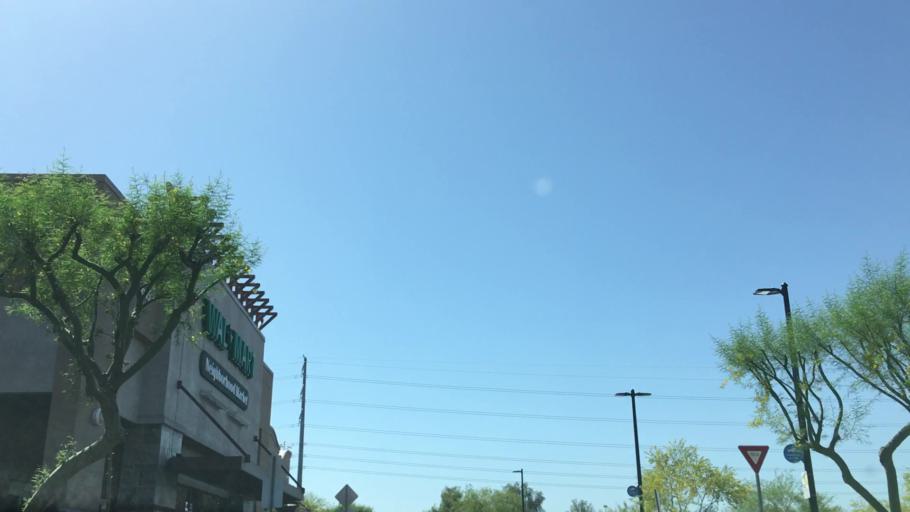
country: US
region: Arizona
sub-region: Maricopa County
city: Peoria
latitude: 33.5806
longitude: -112.2014
